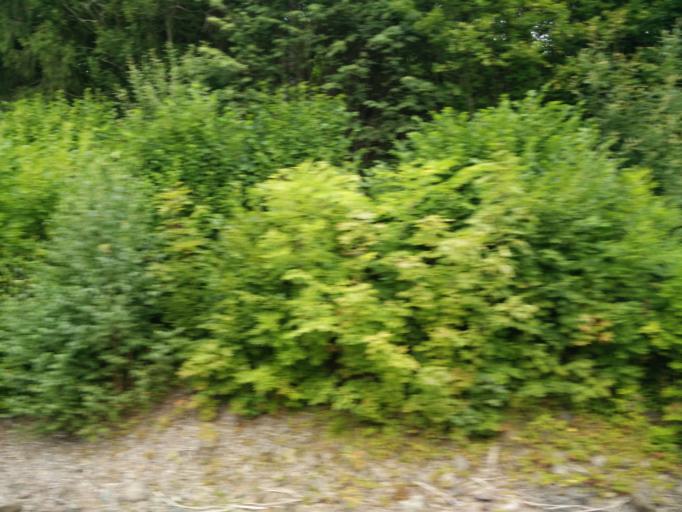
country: NO
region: Akershus
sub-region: Baerum
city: Lysaker
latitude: 59.9400
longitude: 10.6158
